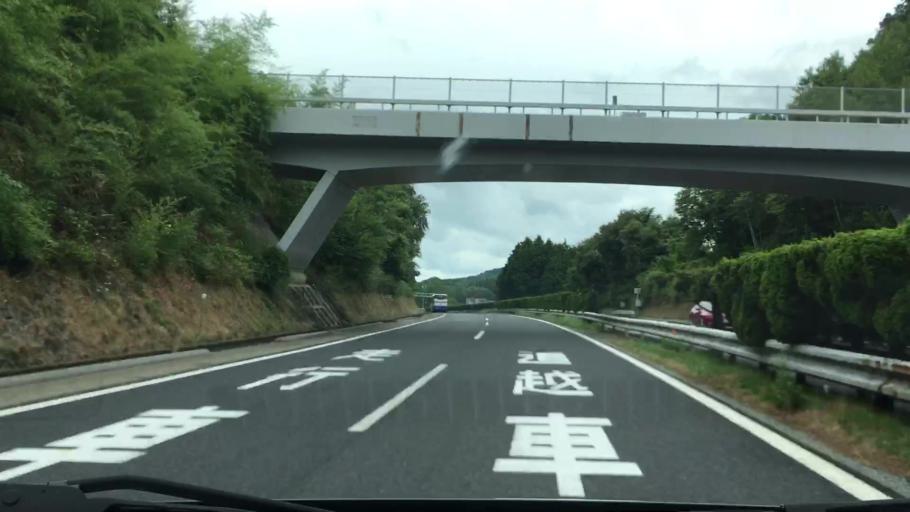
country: JP
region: Okayama
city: Tsuyama
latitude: 35.0313
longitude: 134.1532
